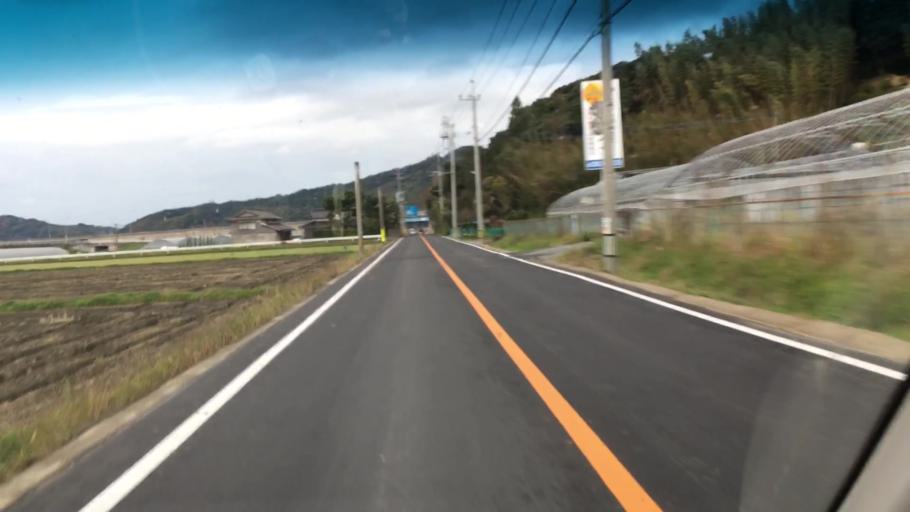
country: JP
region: Fukuoka
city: Maebaru-chuo
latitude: 33.5286
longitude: 130.1896
